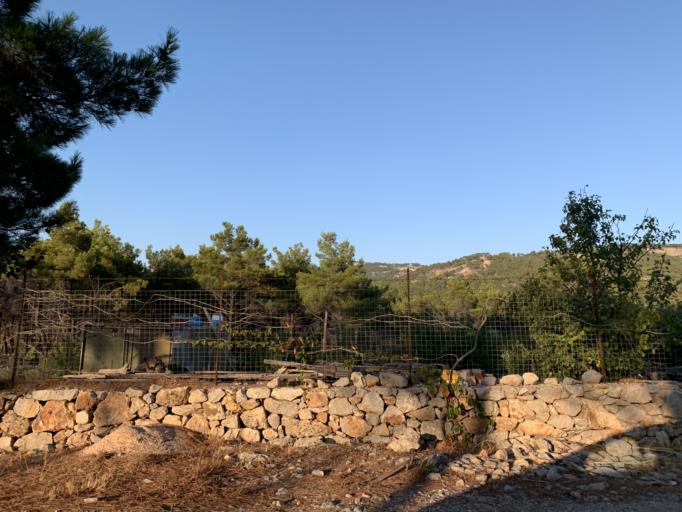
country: GR
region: North Aegean
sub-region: Chios
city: Vrontados
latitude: 38.3813
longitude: 26.0183
